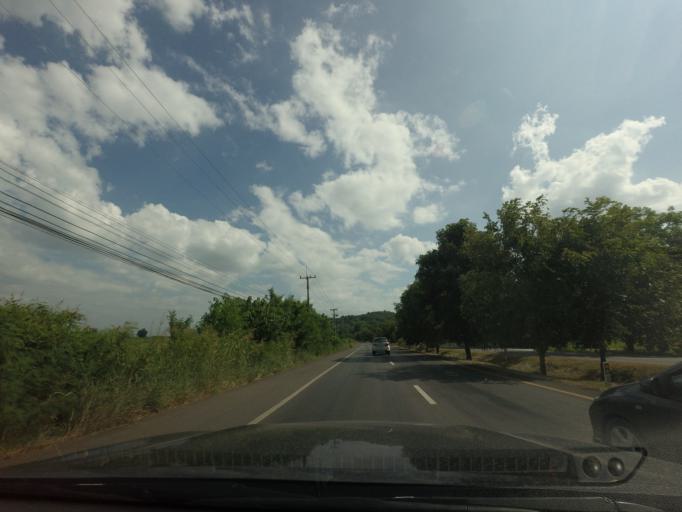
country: TH
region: Phetchabun
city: Wichian Buri
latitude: 15.6320
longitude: 101.0476
